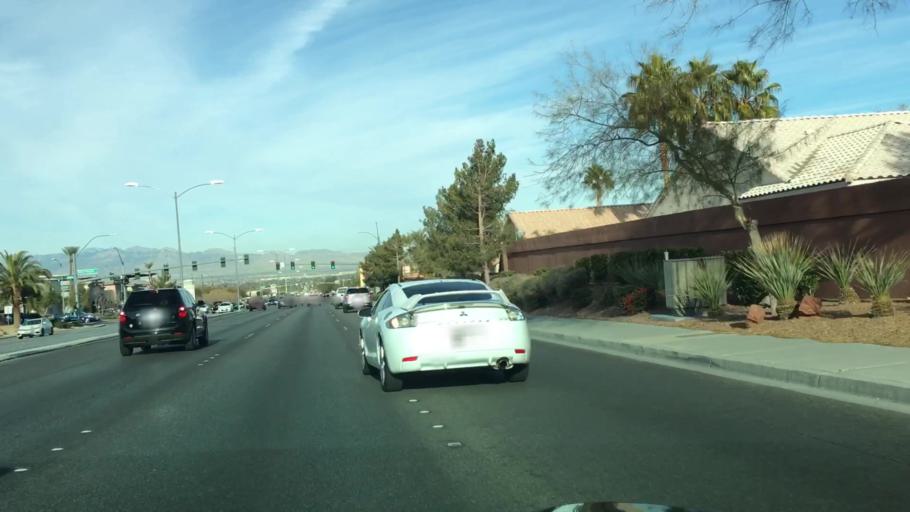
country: US
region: Nevada
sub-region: Clark County
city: Whitney
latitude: 36.0038
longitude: -115.1101
